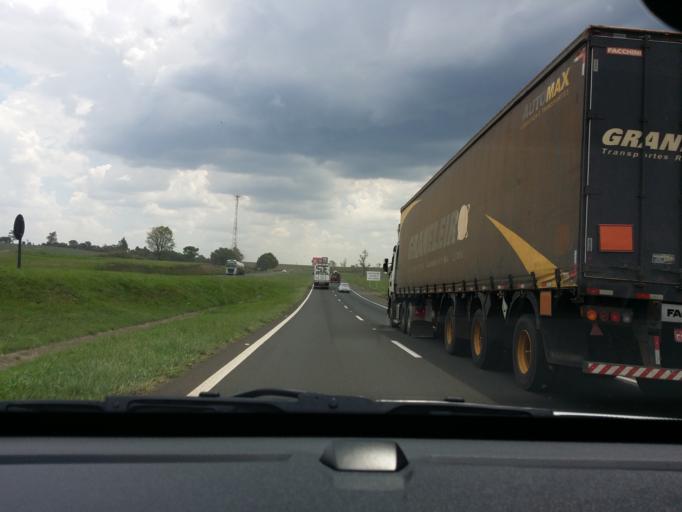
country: BR
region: Sao Paulo
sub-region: Rio Claro
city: Rio Claro
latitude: -22.3520
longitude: -47.6476
